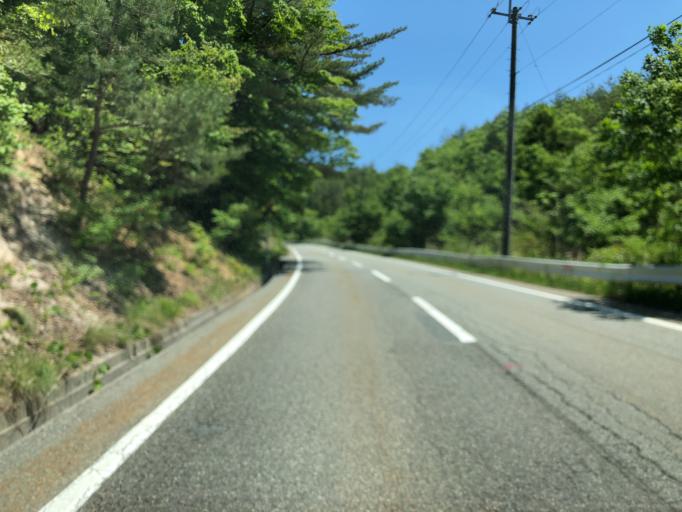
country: JP
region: Fukushima
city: Namie
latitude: 37.5214
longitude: 140.7876
